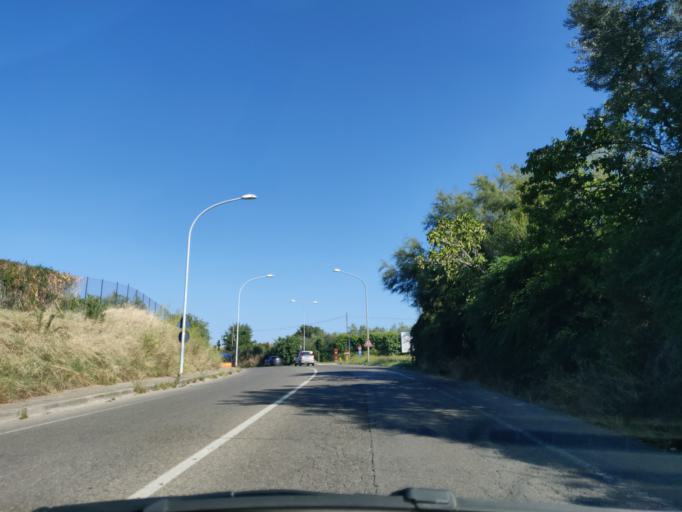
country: IT
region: Latium
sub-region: Provincia di Viterbo
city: Viterbo
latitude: 42.4177
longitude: 12.0974
